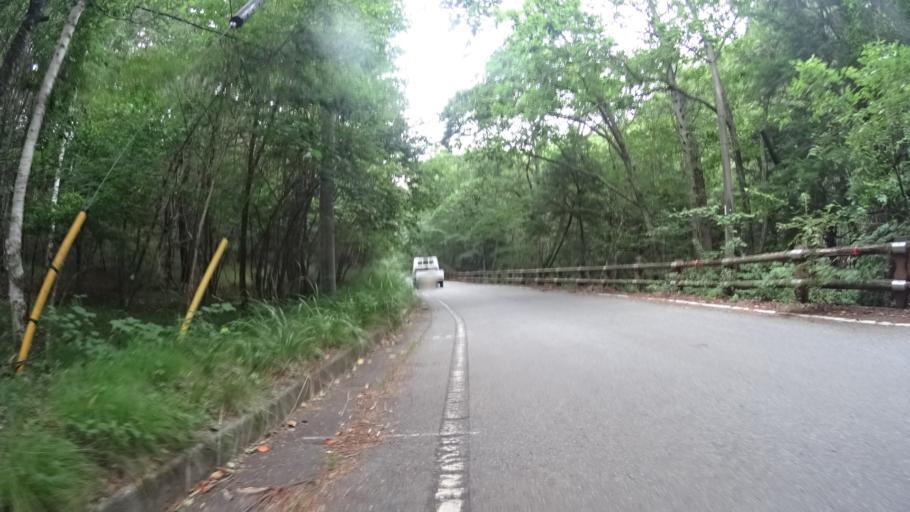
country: JP
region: Yamanashi
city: Nirasaki
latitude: 35.8915
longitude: 138.5654
